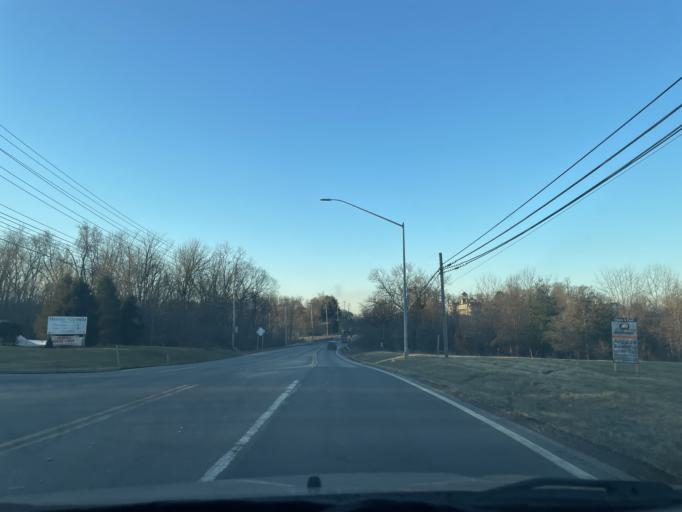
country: US
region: Maryland
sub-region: Frederick County
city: Ballenger Creek
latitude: 39.3660
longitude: -77.4161
